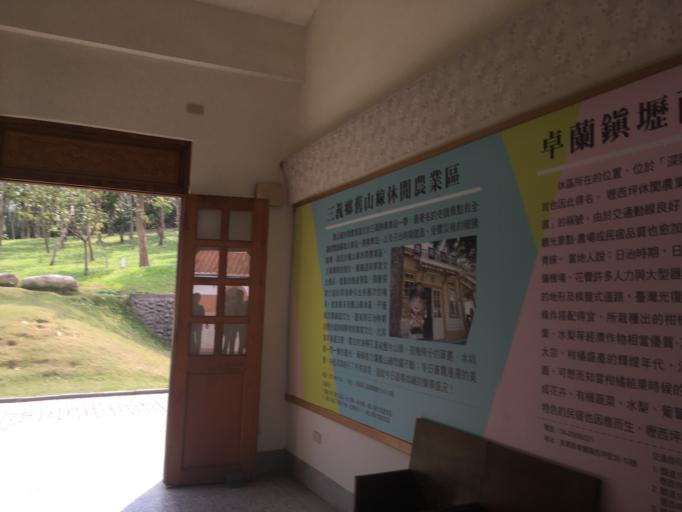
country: TW
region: Taiwan
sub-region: Miaoli
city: Miaoli
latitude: 24.4710
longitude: 120.8013
